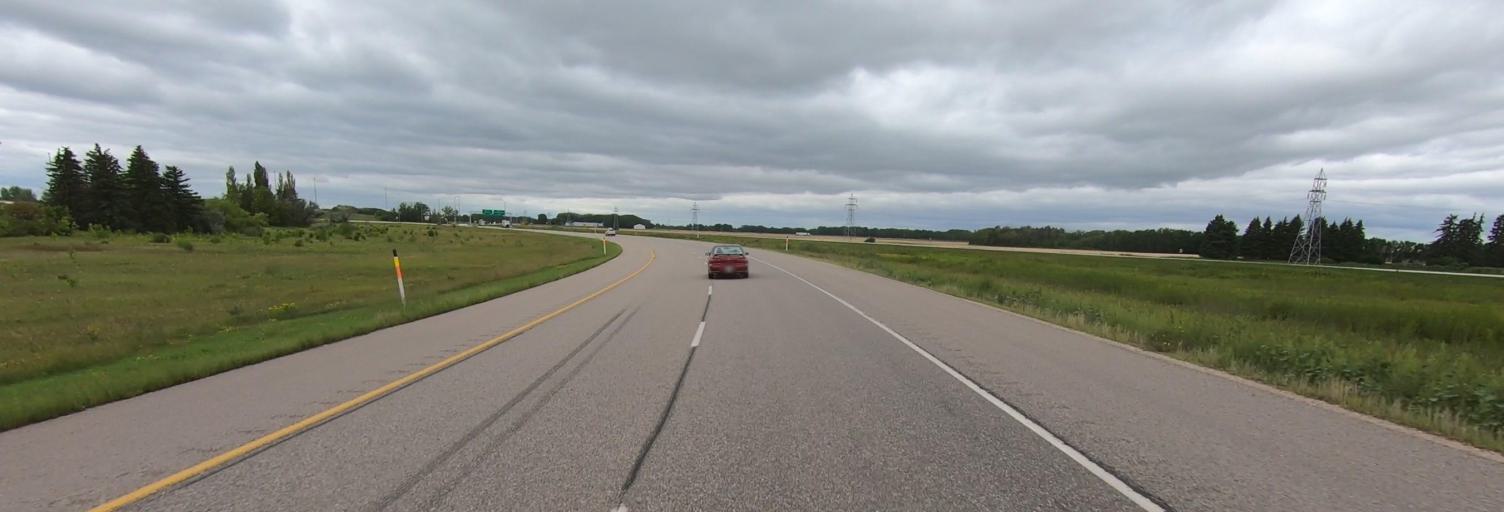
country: CA
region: Manitoba
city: Portage la Prairie
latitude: 49.9761
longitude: -98.2214
